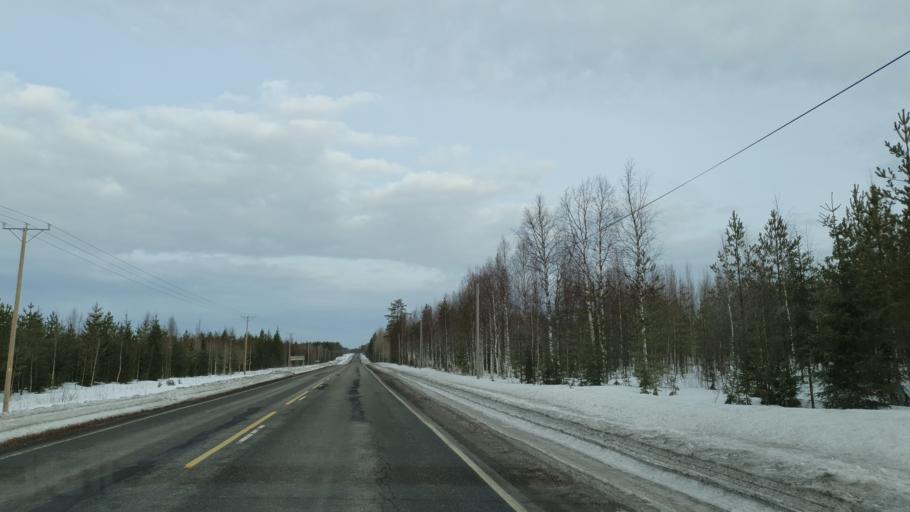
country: FI
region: Kainuu
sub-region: Kajaani
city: Vuokatti
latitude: 64.2053
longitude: 28.1522
